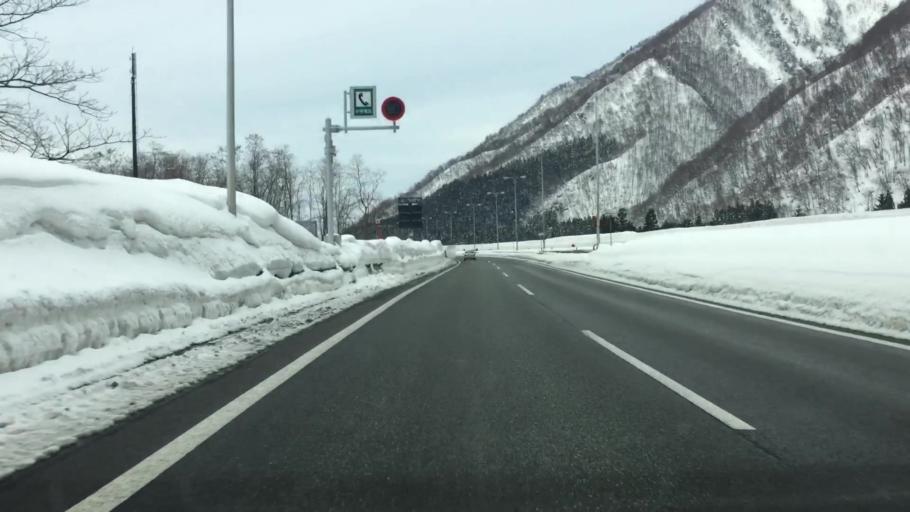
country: JP
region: Niigata
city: Shiozawa
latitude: 36.8717
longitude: 138.8648
